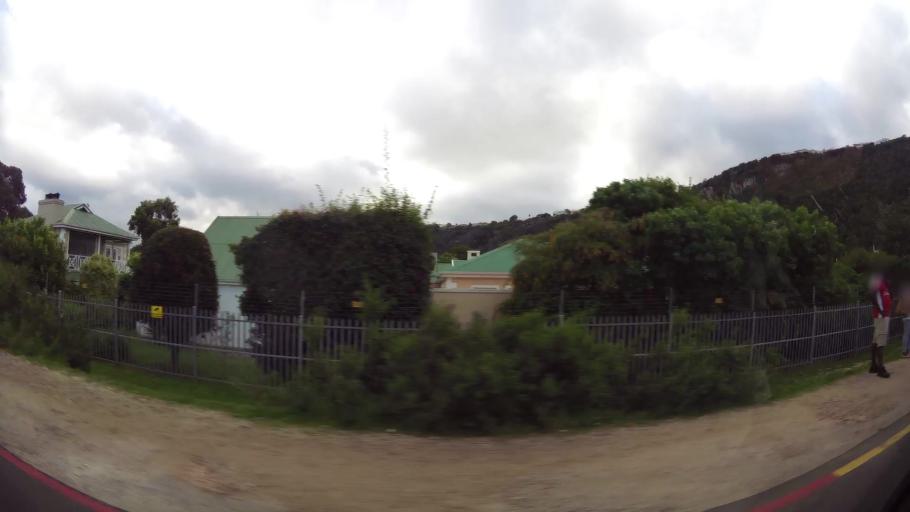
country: ZA
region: Western Cape
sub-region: Eden District Municipality
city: Plettenberg Bay
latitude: -34.0616
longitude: 23.3718
